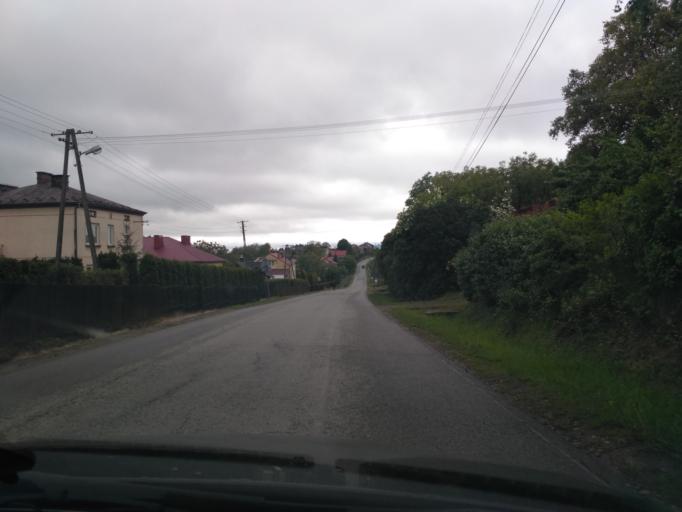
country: PL
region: Subcarpathian Voivodeship
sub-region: Powiat jasielski
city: Jaslo
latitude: 49.8027
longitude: 21.5142
